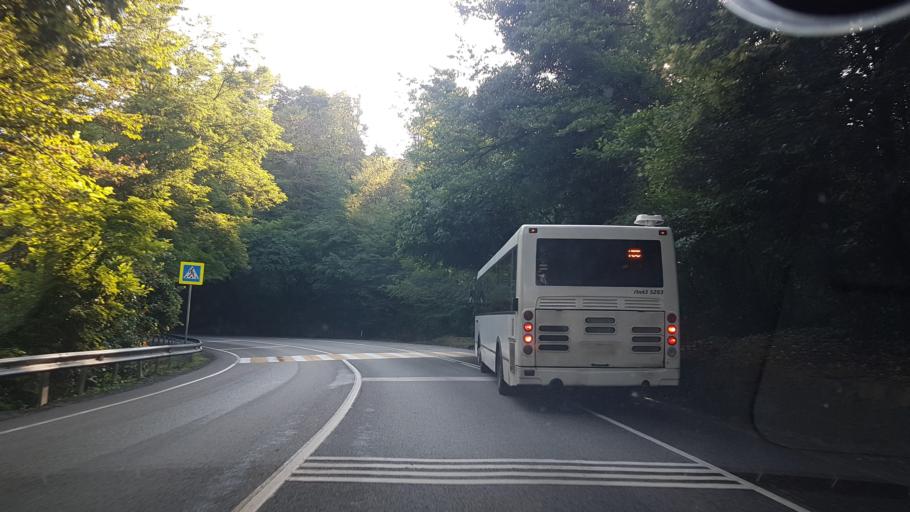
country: RU
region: Krasnodarskiy
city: Vardane
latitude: 43.7900
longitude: 39.4804
